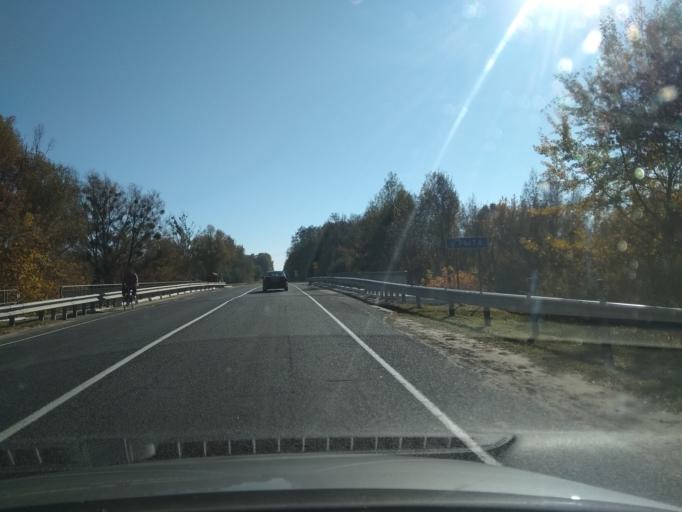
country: BY
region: Brest
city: Malaryta
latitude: 51.9257
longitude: 24.0724
